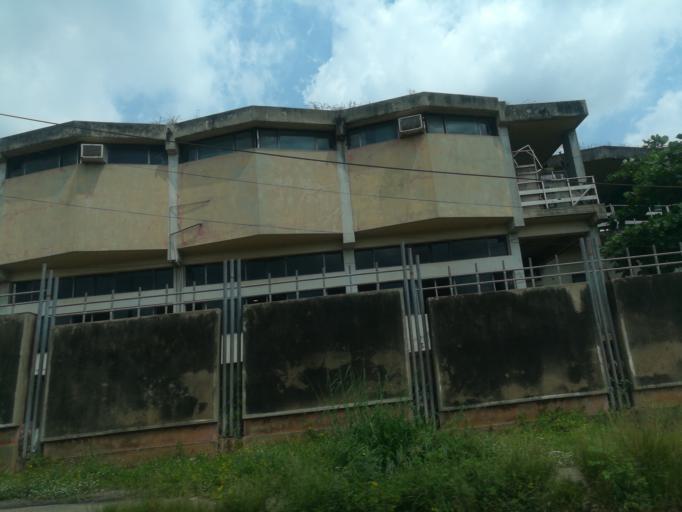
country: NG
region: Oyo
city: Ibadan
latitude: 7.3975
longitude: 3.8839
